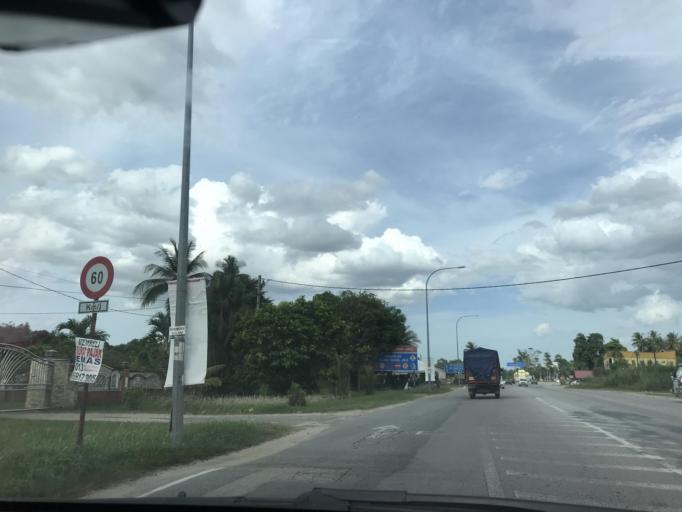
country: MY
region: Kelantan
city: Kampung Lemal
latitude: 6.0342
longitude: 102.1568
